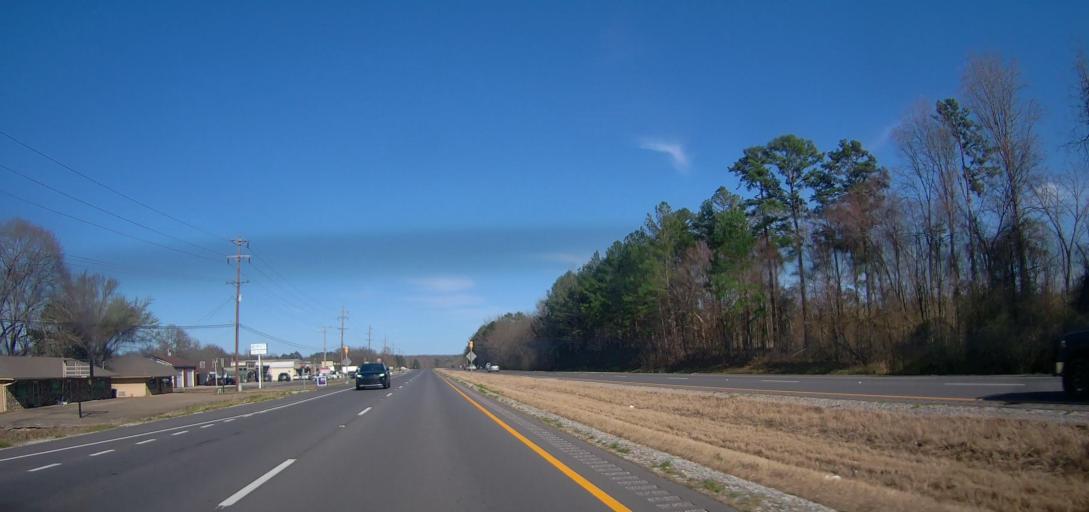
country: US
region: Alabama
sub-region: Lauderdale County
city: Killen
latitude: 34.8579
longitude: -87.5392
